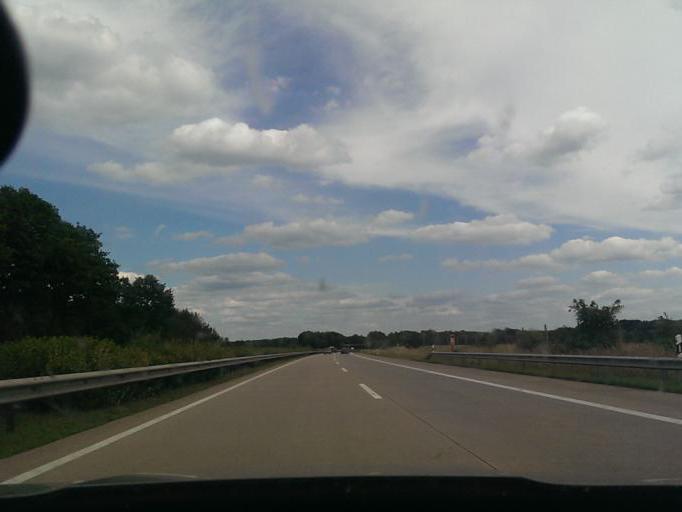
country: DE
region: Lower Saxony
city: Kirchlinteln
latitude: 52.9276
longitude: 9.3241
